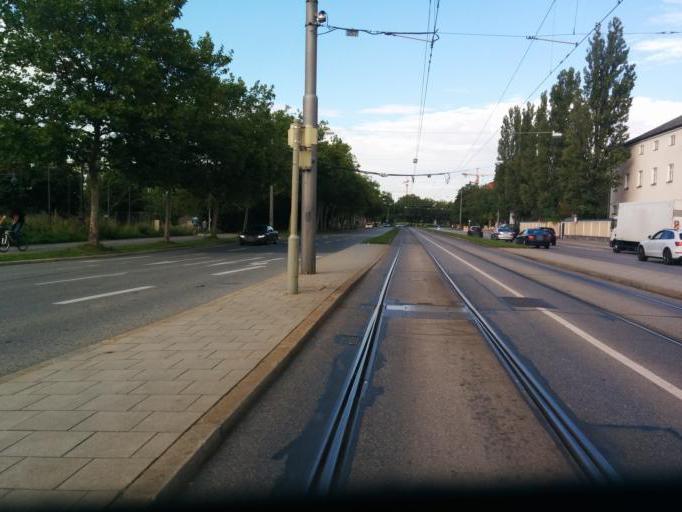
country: DE
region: Bavaria
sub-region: Upper Bavaria
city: Munich
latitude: 48.1599
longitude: 11.5480
